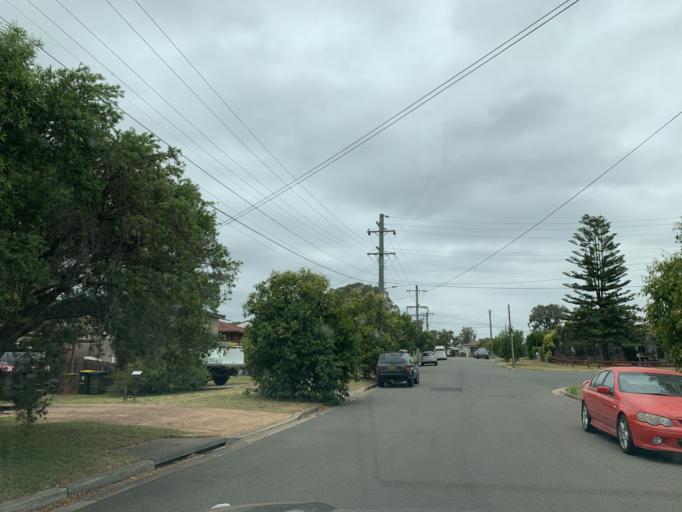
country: AU
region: New South Wales
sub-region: Blacktown
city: Blacktown
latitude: -33.7780
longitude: 150.8976
